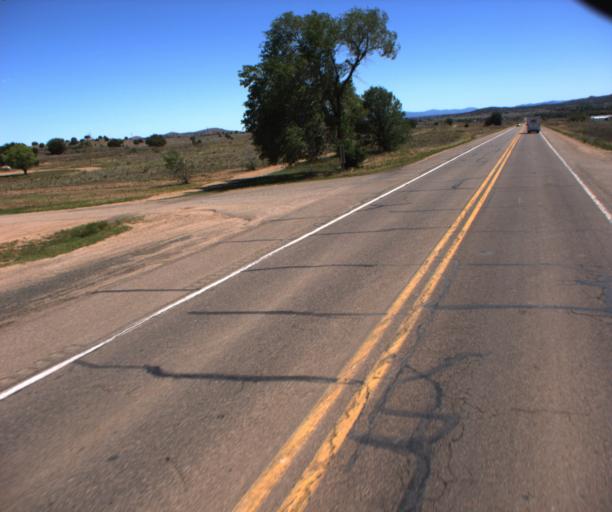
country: US
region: Arizona
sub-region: Yavapai County
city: Paulden
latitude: 34.8856
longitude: -112.4680
